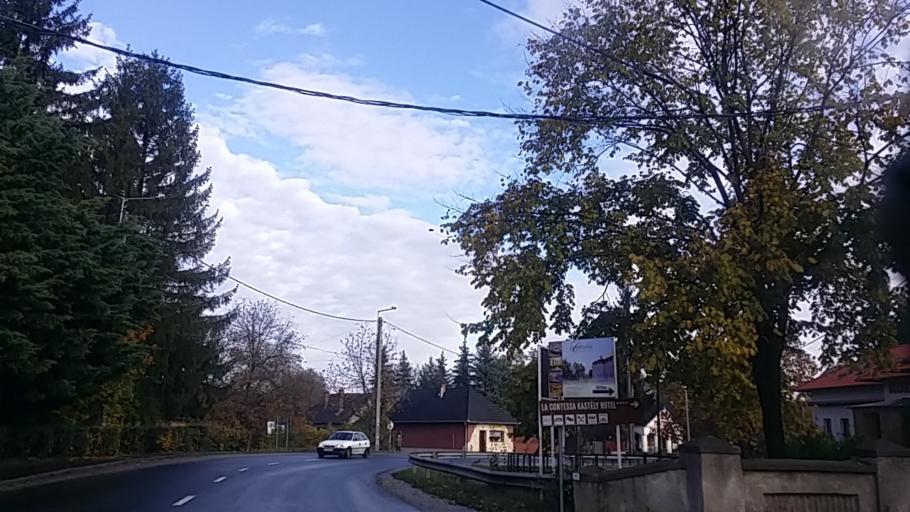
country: HU
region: Heves
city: Szilvasvarad
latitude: 48.1033
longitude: 20.3884
